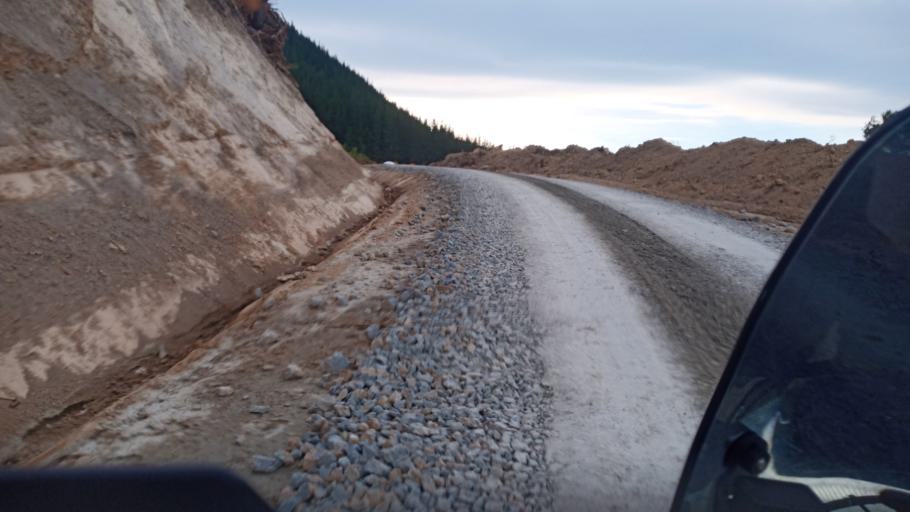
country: NZ
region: Gisborne
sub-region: Gisborne District
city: Gisborne
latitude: -38.4653
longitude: 177.9512
